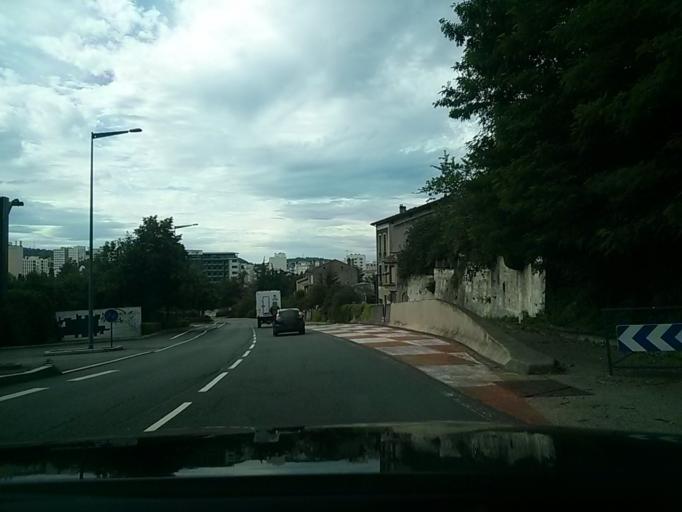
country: FR
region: Rhone-Alpes
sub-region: Departement de la Loire
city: Saint-Etienne
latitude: 45.4086
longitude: 4.4002
